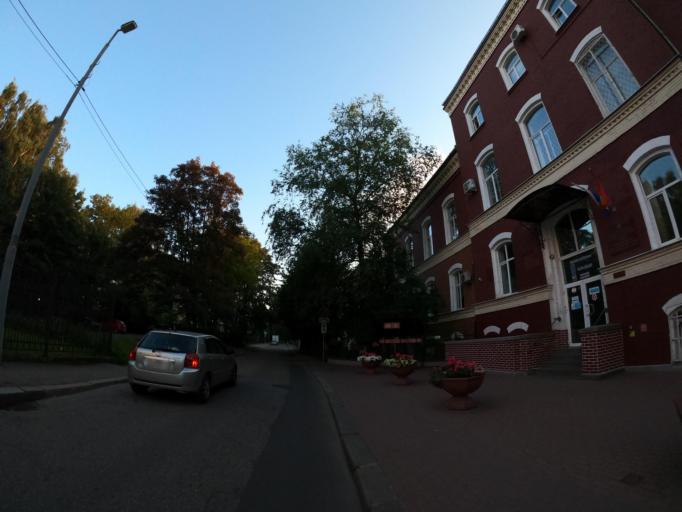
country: RU
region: Kaliningrad
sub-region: Gorod Kaliningrad
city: Kaliningrad
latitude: 54.7134
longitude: 20.5018
